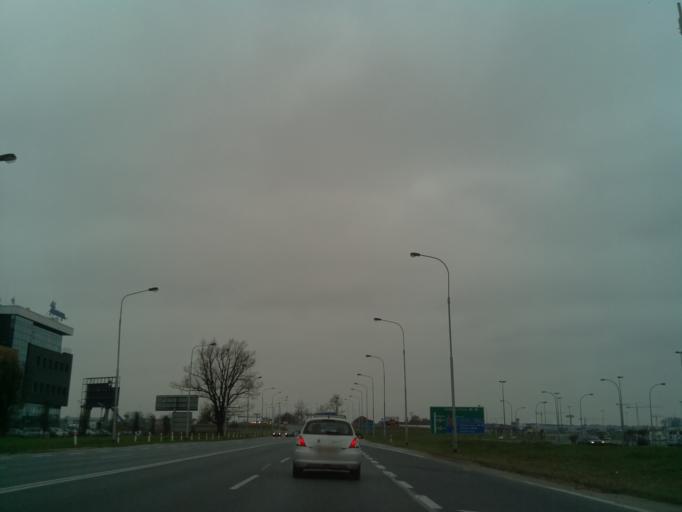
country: PL
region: Lower Silesian Voivodeship
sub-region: Powiat wroclawski
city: Bielany Wroclawskie
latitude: 51.0531
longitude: 16.9776
